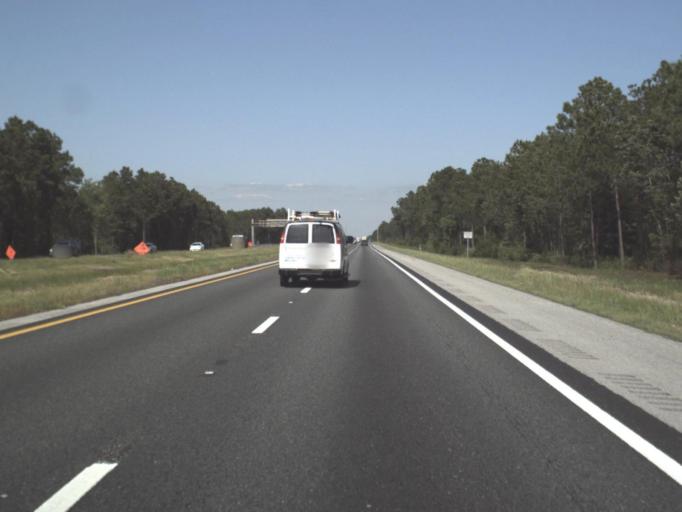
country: US
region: Florida
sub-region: Santa Rosa County
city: Bagdad
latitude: 30.5431
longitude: -87.0659
